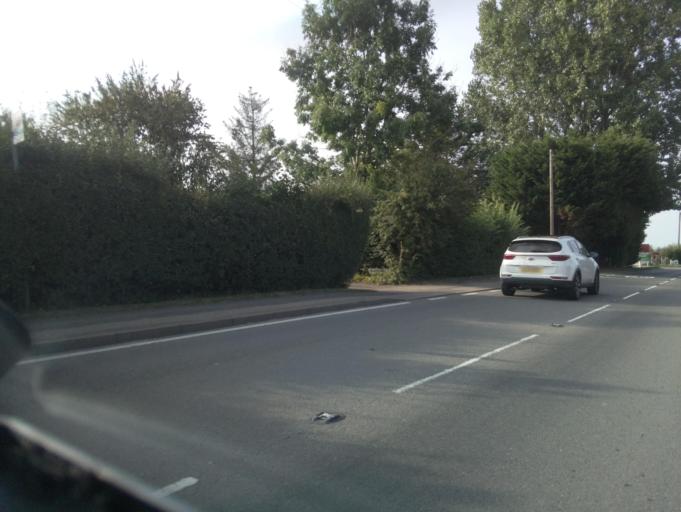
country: GB
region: England
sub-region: Warwickshire
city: Alcester
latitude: 52.2298
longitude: -1.8805
